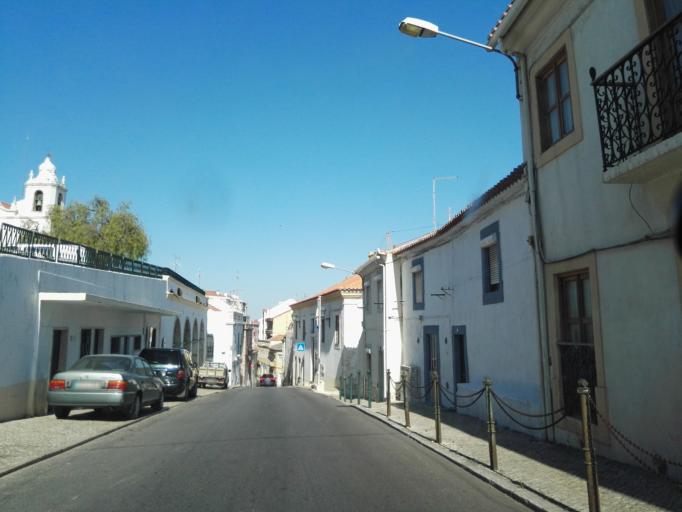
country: PT
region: Lisbon
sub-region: Vila Franca de Xira
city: Sobralinho
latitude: 38.8994
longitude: -9.0390
